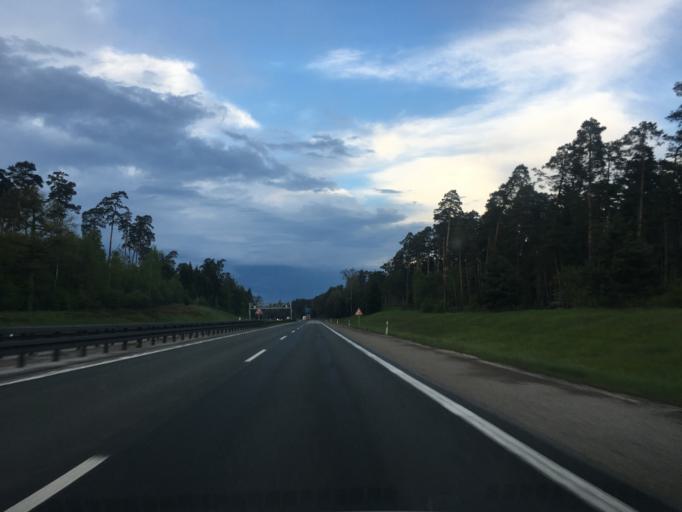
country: DE
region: Bavaria
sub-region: Regierungsbezirk Mittelfranken
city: Leinburg
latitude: 49.4405
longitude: 11.2687
